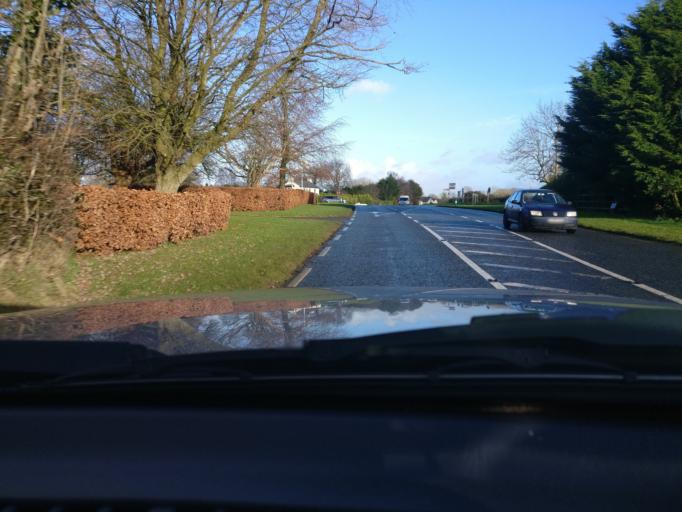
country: IE
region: Leinster
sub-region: An Iarmhi
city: An Muileann gCearr
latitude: 53.5140
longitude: -7.3903
